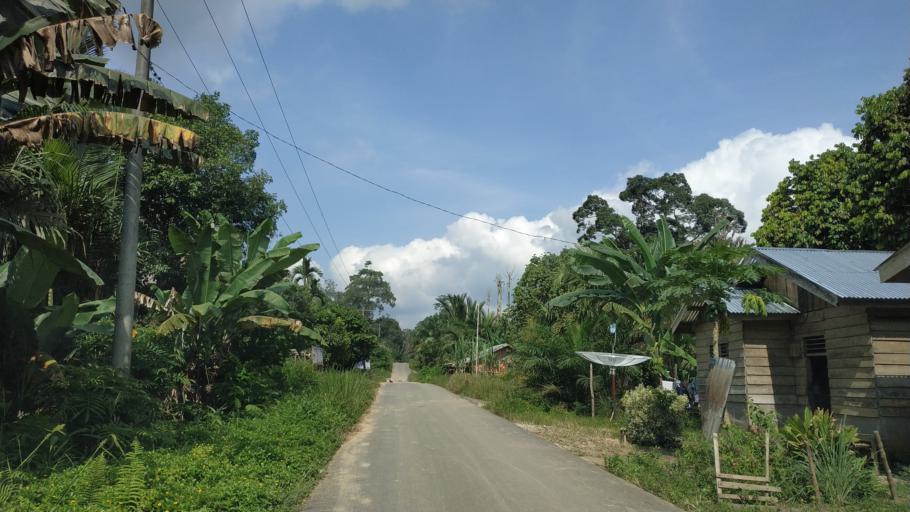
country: ID
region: Riau
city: Pangkalan Kasai
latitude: -0.7263
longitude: 102.4806
